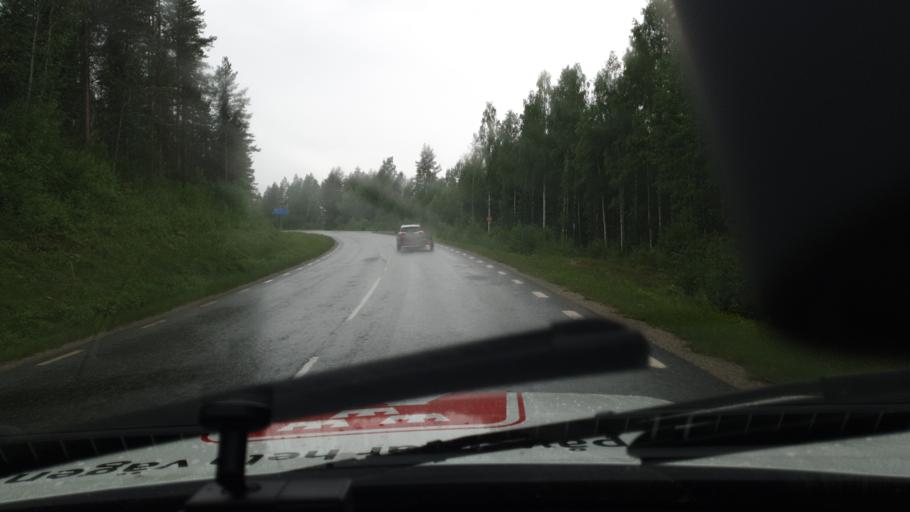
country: SE
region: Vaesterbotten
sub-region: Lycksele Kommun
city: Lycksele
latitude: 64.5067
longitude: 18.8924
